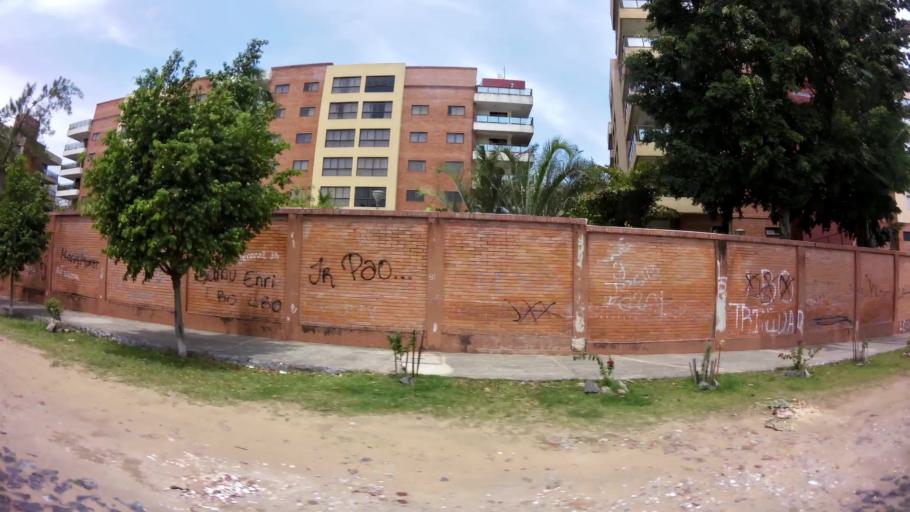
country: PY
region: Asuncion
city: Asuncion
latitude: -25.2657
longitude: -57.5944
